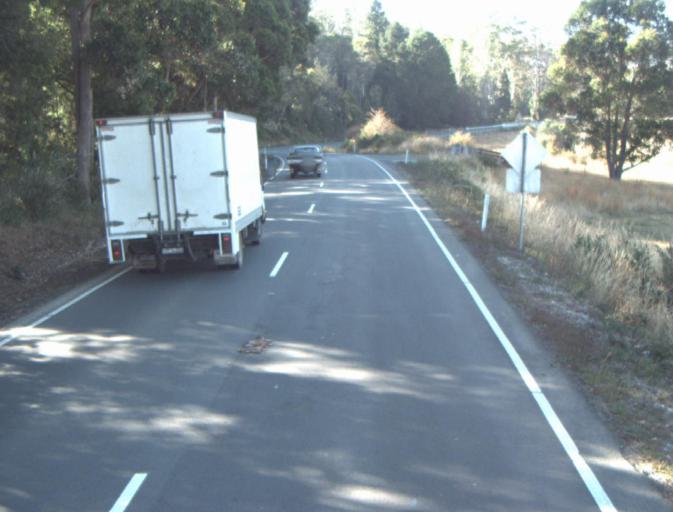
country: AU
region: Tasmania
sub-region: Launceston
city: Mayfield
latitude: -41.2264
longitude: 147.2073
